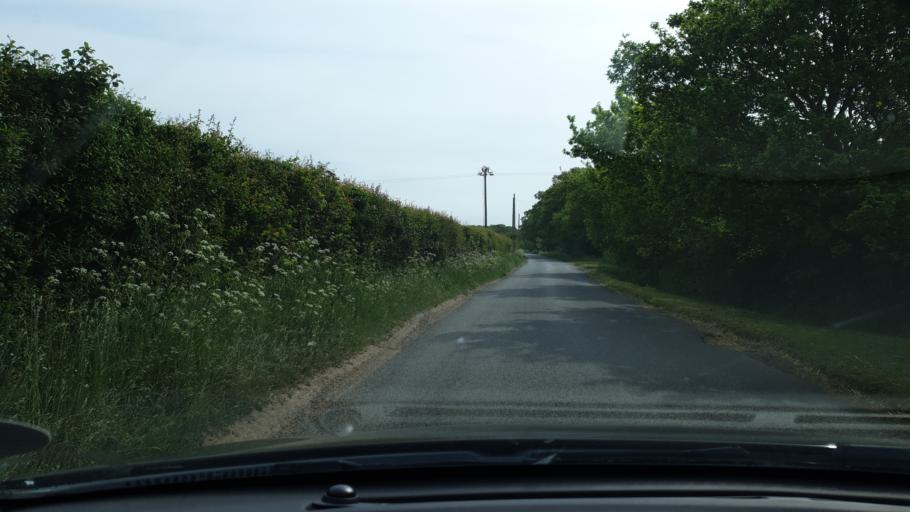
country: GB
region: England
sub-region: Essex
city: Great Bentley
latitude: 51.8400
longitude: 1.0984
